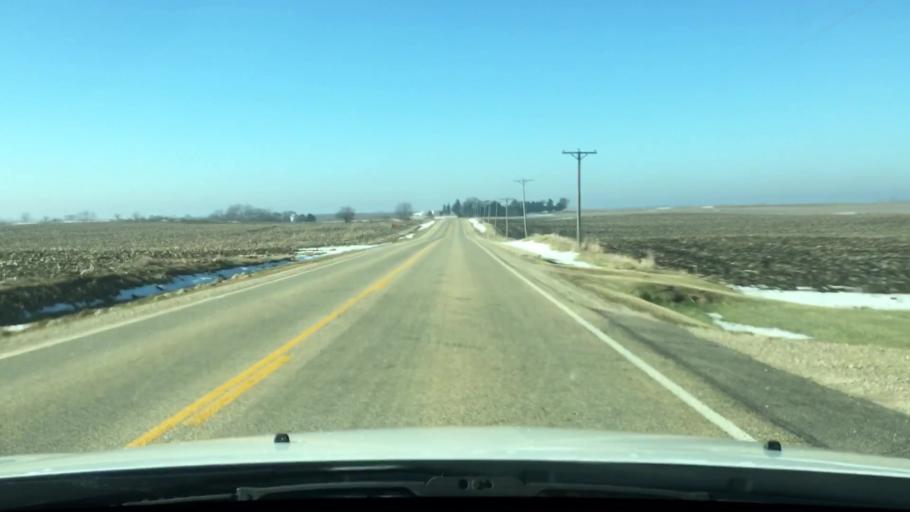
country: US
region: Illinois
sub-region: DeKalb County
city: Malta
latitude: 41.8485
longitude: -88.9297
